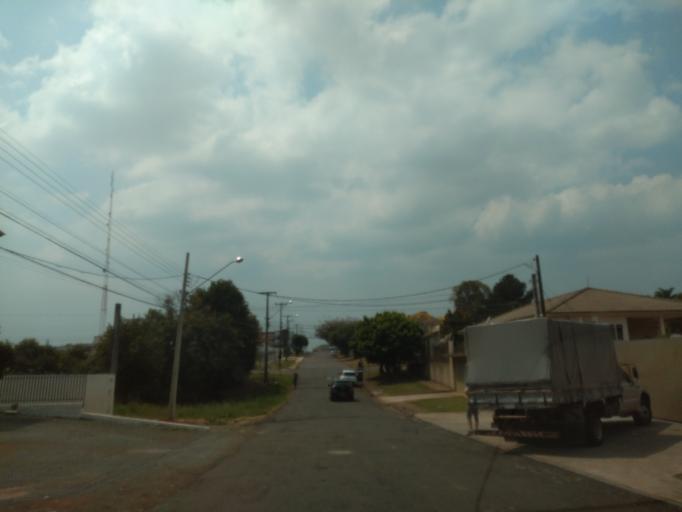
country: BR
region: Parana
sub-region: Guarapuava
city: Guarapuava
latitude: -25.3872
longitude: -51.4800
